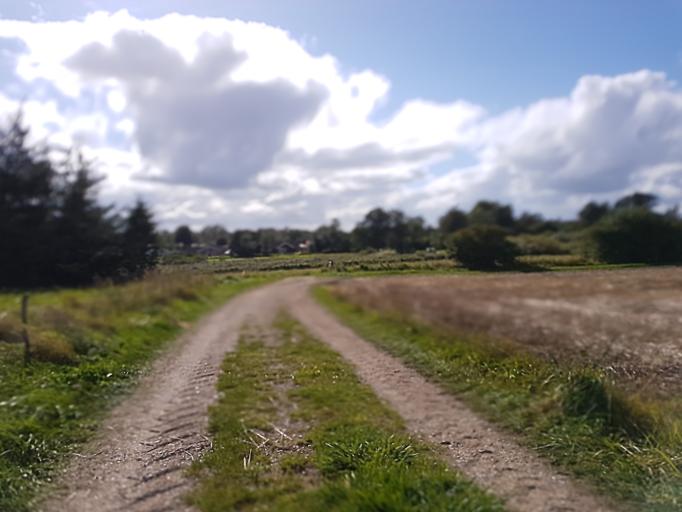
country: DK
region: Zealand
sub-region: Roskilde Kommune
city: Jyllinge
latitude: 55.7793
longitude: 12.0956
